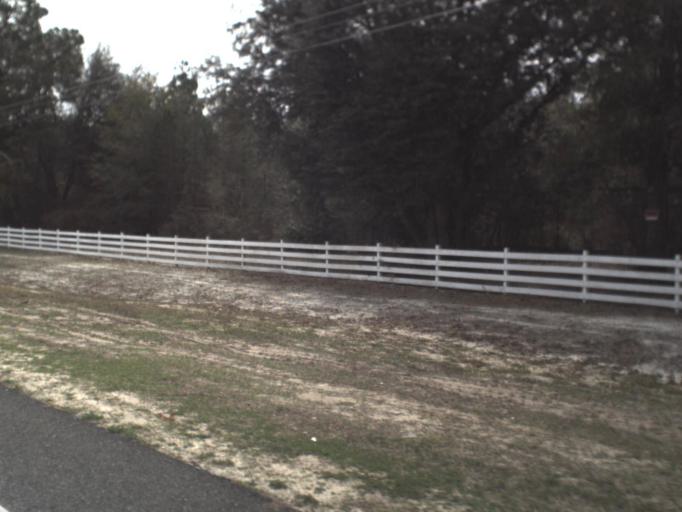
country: US
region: Florida
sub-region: Bay County
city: Youngstown
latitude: 30.4565
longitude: -85.4243
